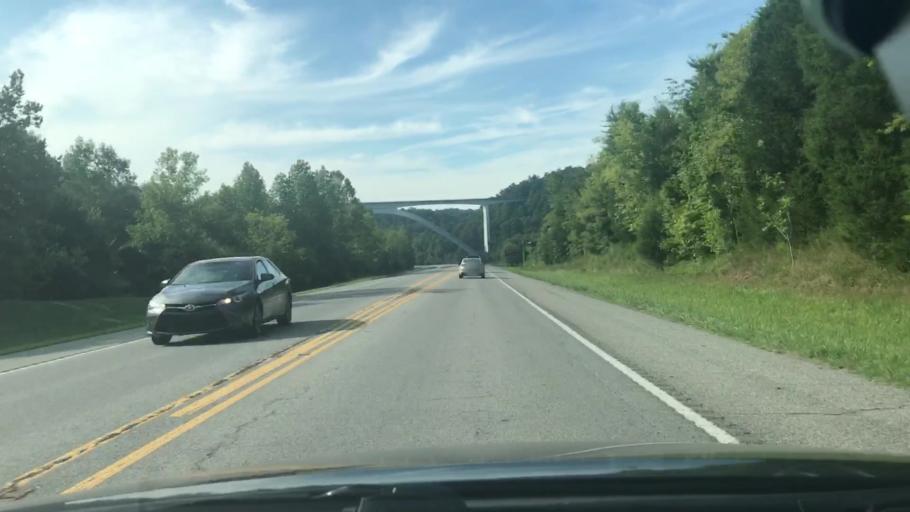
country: US
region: Tennessee
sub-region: Williamson County
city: Franklin
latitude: 35.9814
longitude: -86.9882
